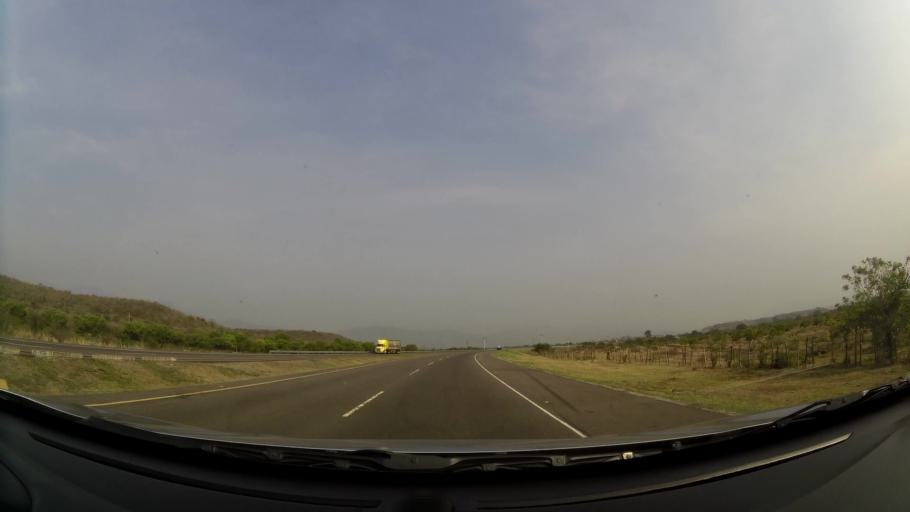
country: HN
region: Comayagua
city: Comayagua
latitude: 14.4361
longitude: -87.6556
